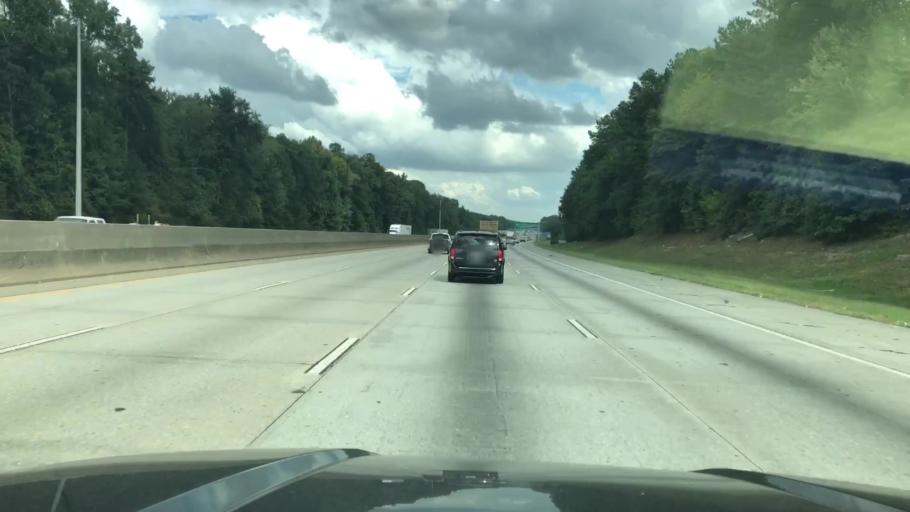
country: US
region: Georgia
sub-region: Fulton County
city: Union City
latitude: 33.5718
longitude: -84.5290
